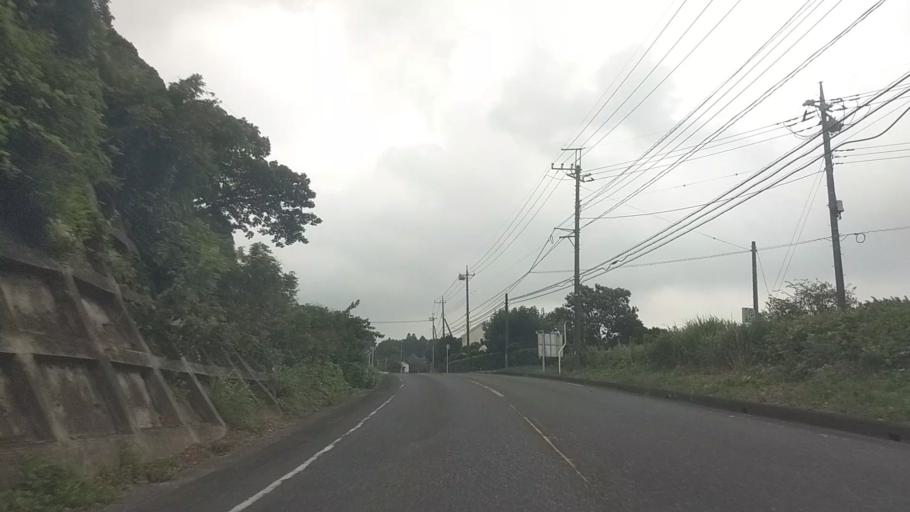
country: JP
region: Chiba
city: Ohara
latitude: 35.2821
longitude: 140.2892
